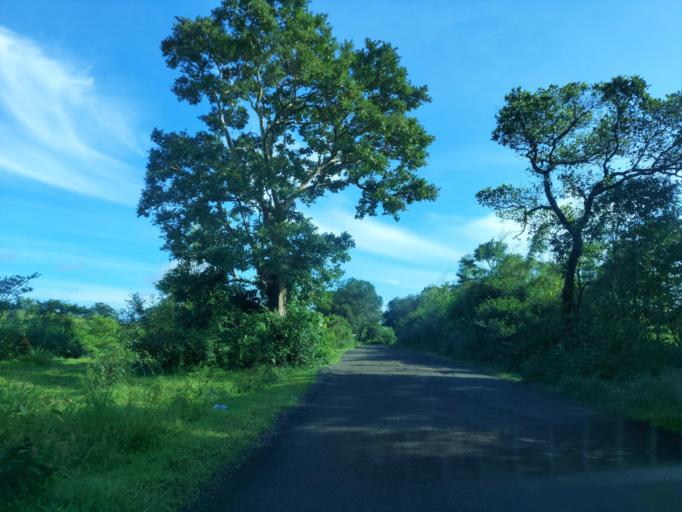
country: IN
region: Maharashtra
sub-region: Kolhapur
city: Ajra
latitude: 16.0122
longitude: 74.0492
